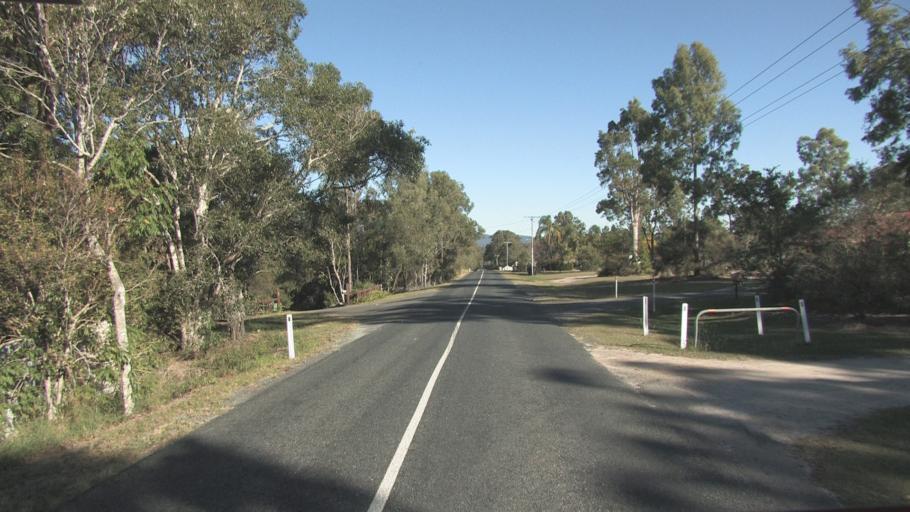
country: AU
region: Queensland
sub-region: Logan
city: Logan Reserve
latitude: -27.7295
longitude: 153.1046
